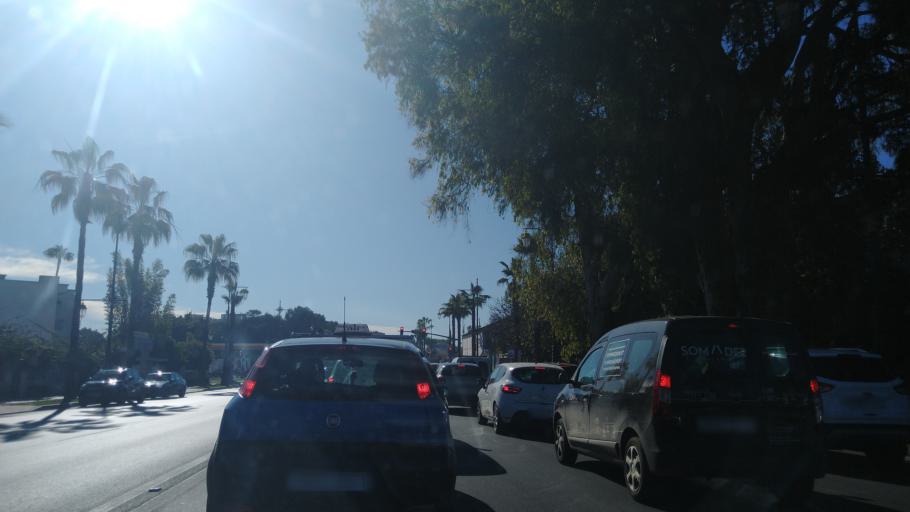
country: MA
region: Rabat-Sale-Zemmour-Zaer
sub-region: Rabat
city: Rabat
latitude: 33.9948
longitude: -6.8274
